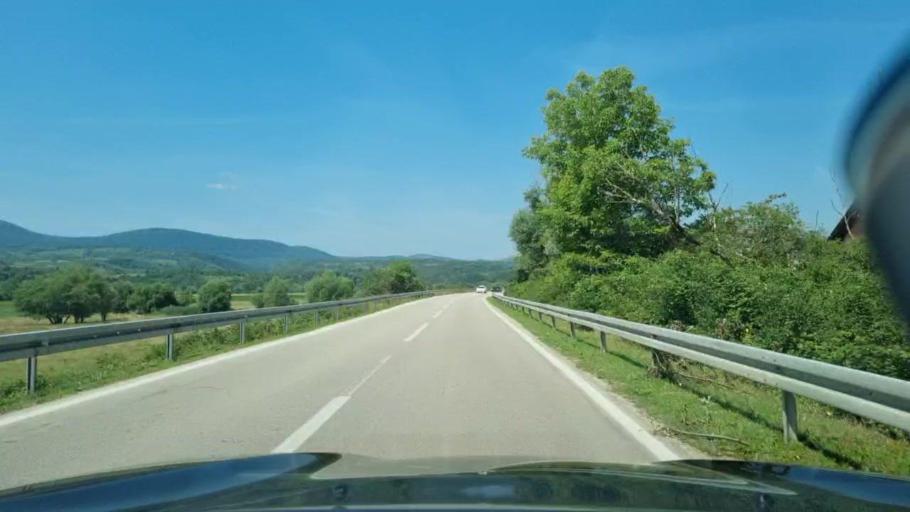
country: BA
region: Federation of Bosnia and Herzegovina
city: Sanski Most
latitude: 44.7171
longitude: 16.7025
